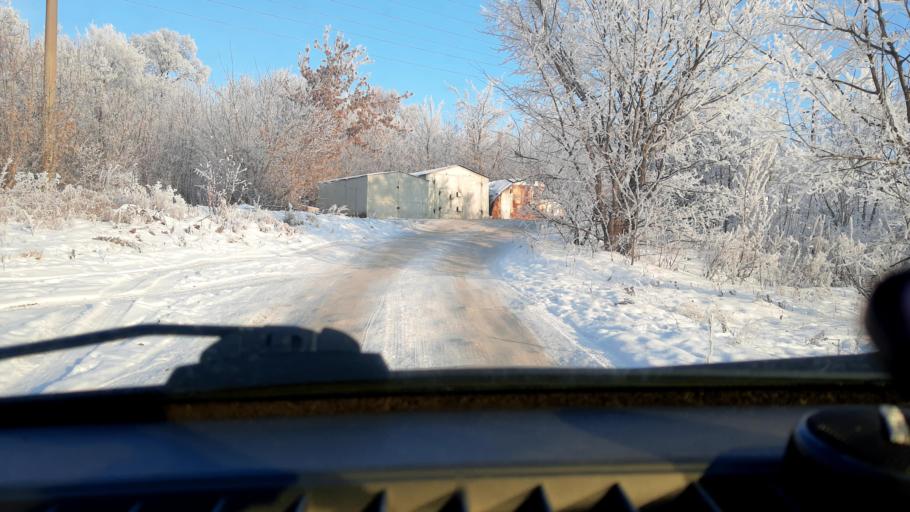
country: RU
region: Bashkortostan
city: Iglino
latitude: 54.7713
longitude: 56.2417
